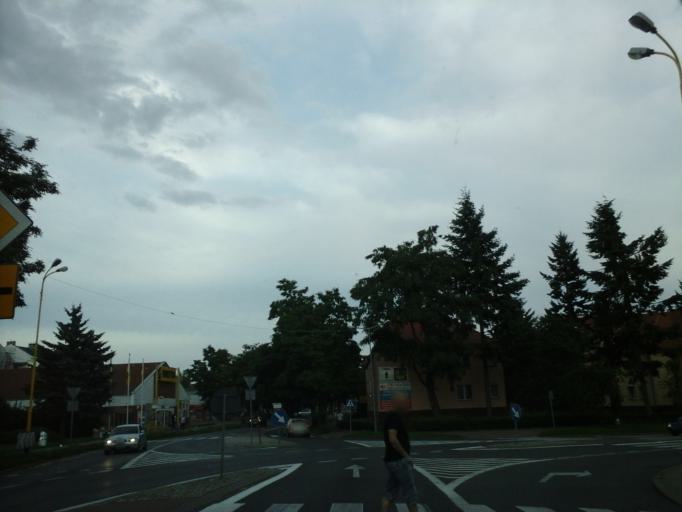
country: PL
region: West Pomeranian Voivodeship
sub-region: Powiat goleniowski
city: Nowogard
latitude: 53.6700
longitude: 15.1218
